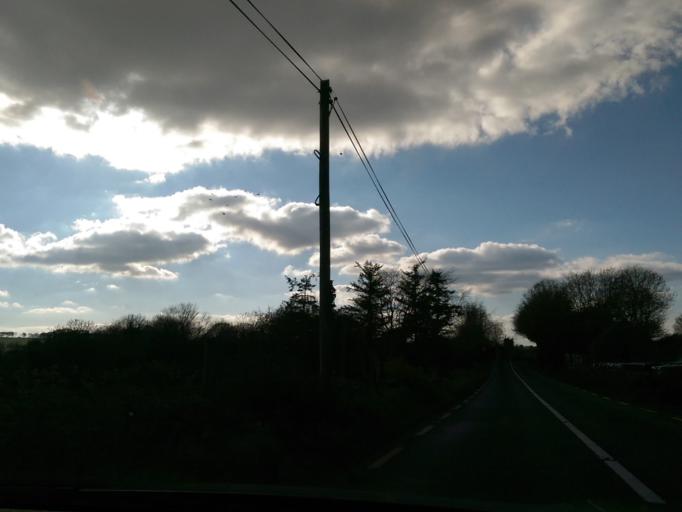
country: IE
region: Connaught
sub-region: County Galway
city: Loughrea
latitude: 53.2018
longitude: -8.4664
